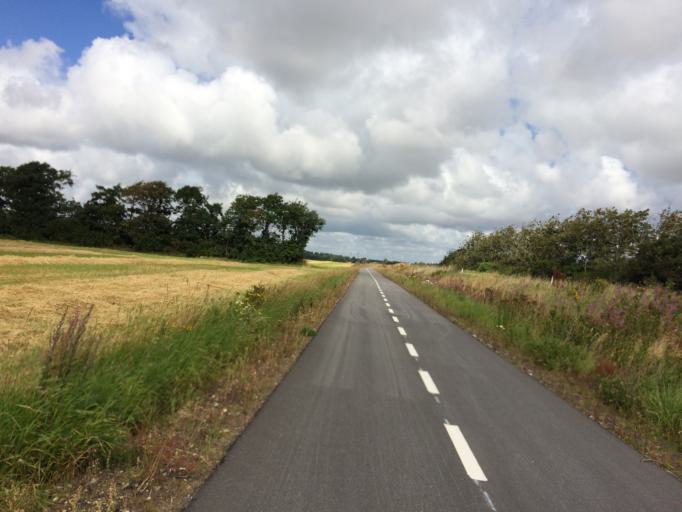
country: DK
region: Central Jutland
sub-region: Holstebro Kommune
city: Ulfborg
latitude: 56.3197
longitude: 8.3402
